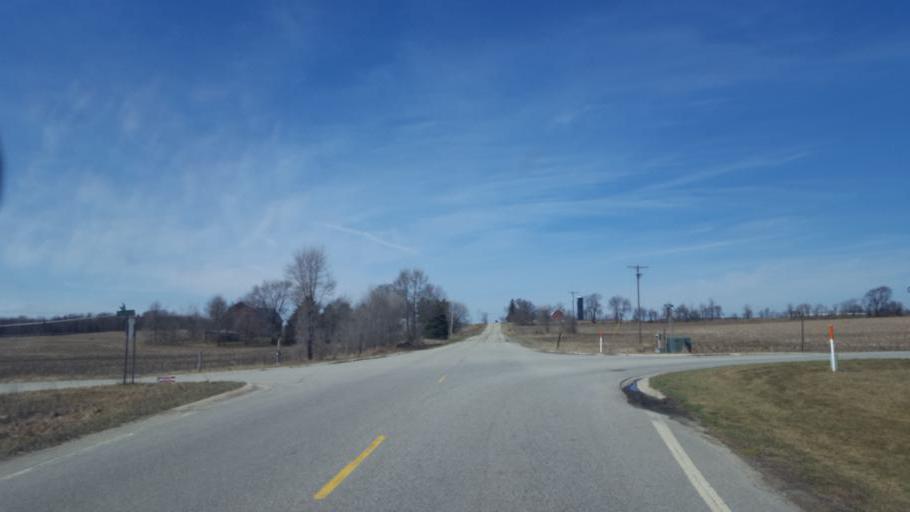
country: US
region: Michigan
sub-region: Montcalm County
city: Edmore
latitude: 43.4662
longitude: -85.0845
